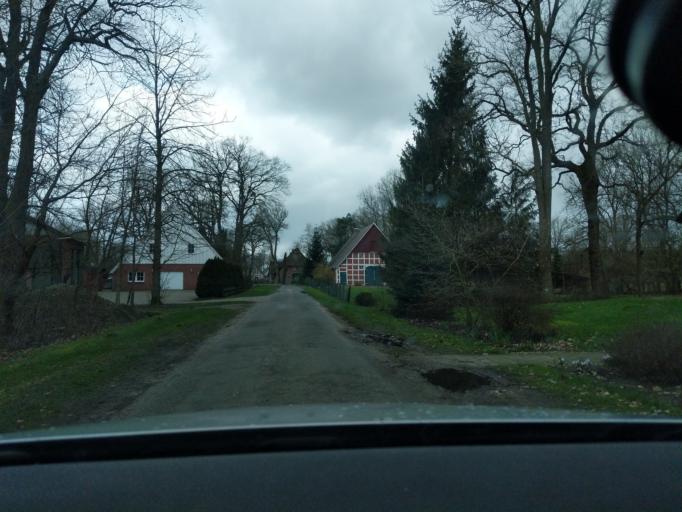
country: DE
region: Lower Saxony
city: Kranenburg
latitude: 53.5957
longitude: 9.1852
